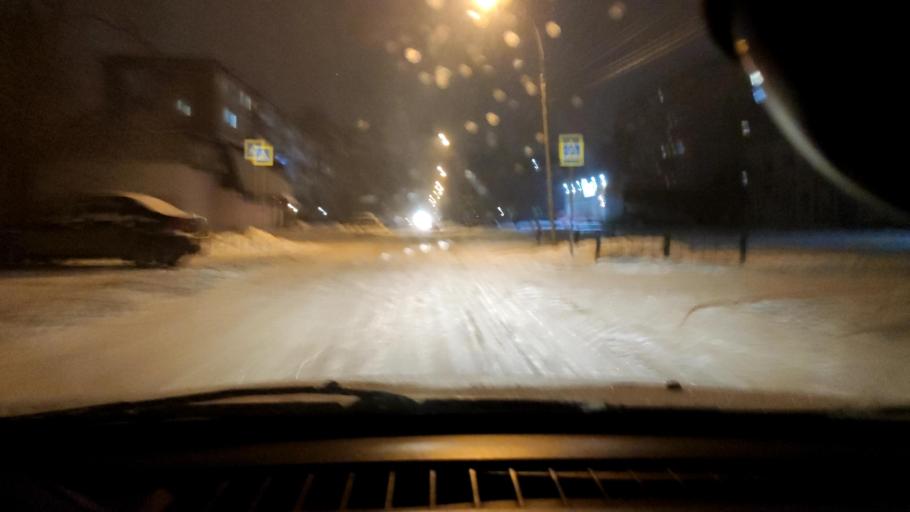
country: RU
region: Perm
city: Overyata
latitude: 58.0093
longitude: 55.9389
